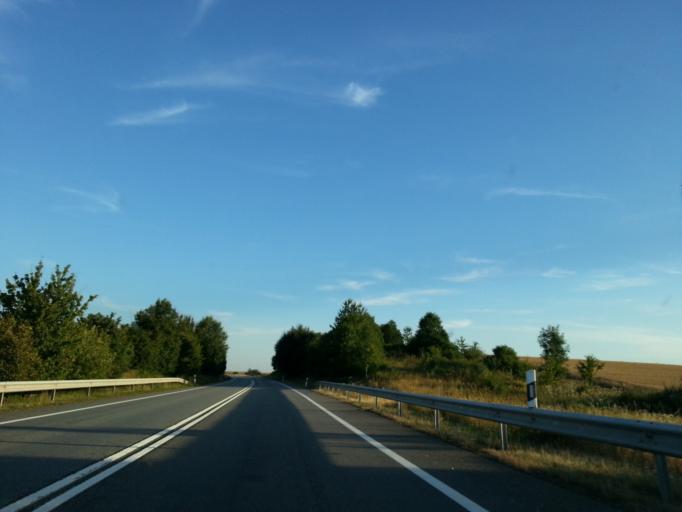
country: DE
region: Rheinland-Pfalz
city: Obernheim-Kirchenarnbach
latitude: 49.3613
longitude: 7.6040
